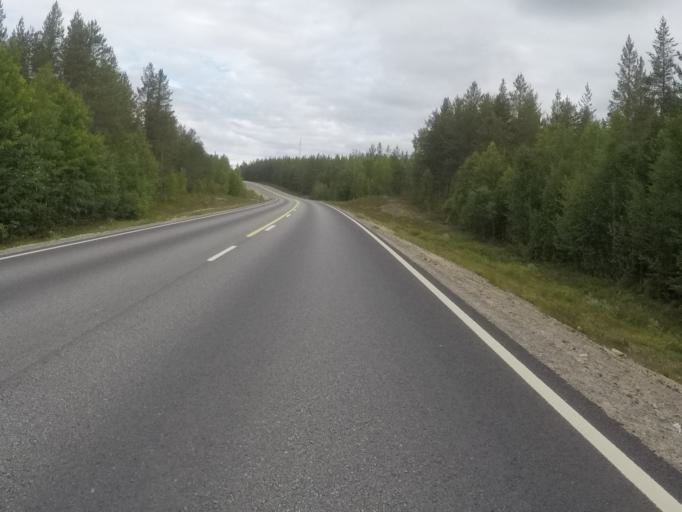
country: FI
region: Lapland
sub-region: Tunturi-Lappi
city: Kolari
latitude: 67.5550
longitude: 23.6083
